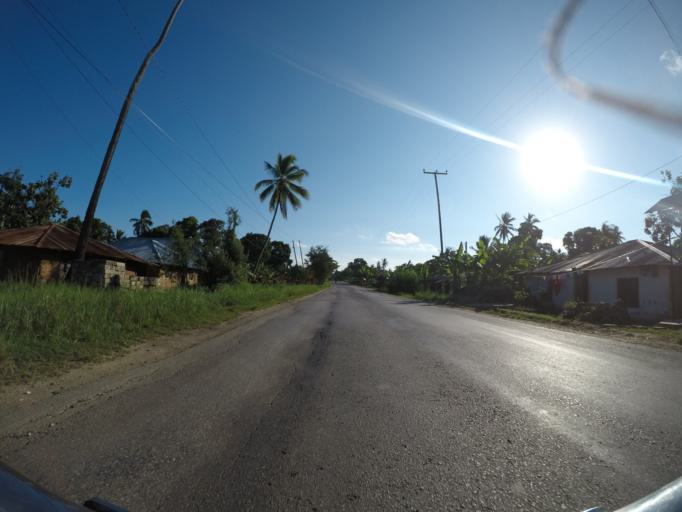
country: TZ
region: Pemba South
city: Chake Chake
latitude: -5.2894
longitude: 39.7617
